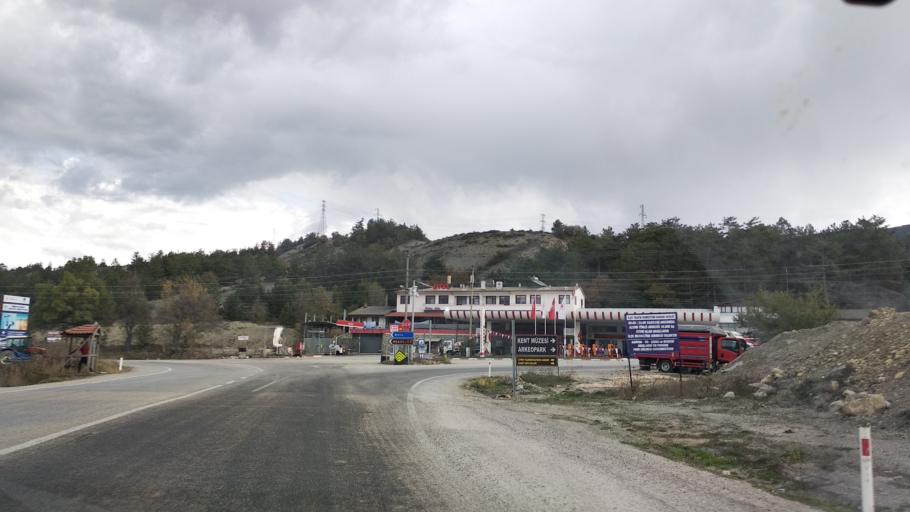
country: TR
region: Bolu
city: Mudurnu
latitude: 40.4898
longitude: 31.2012
